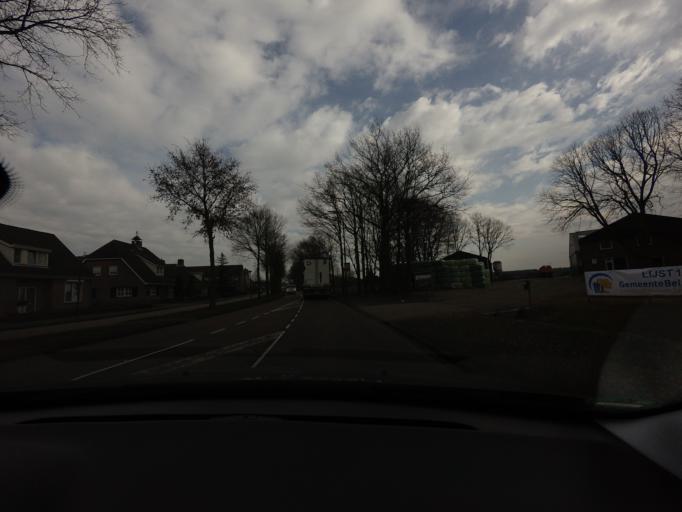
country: NL
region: North Brabant
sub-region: Gemeente Loon op Zand
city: Loon op Zand
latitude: 51.6487
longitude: 5.0211
